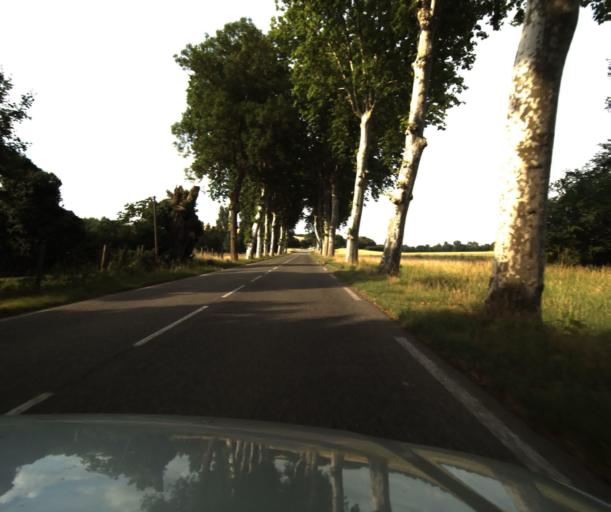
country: FR
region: Midi-Pyrenees
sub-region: Departement du Tarn-et-Garonne
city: Beaumont-de-Lomagne
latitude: 43.8556
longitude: 0.9453
